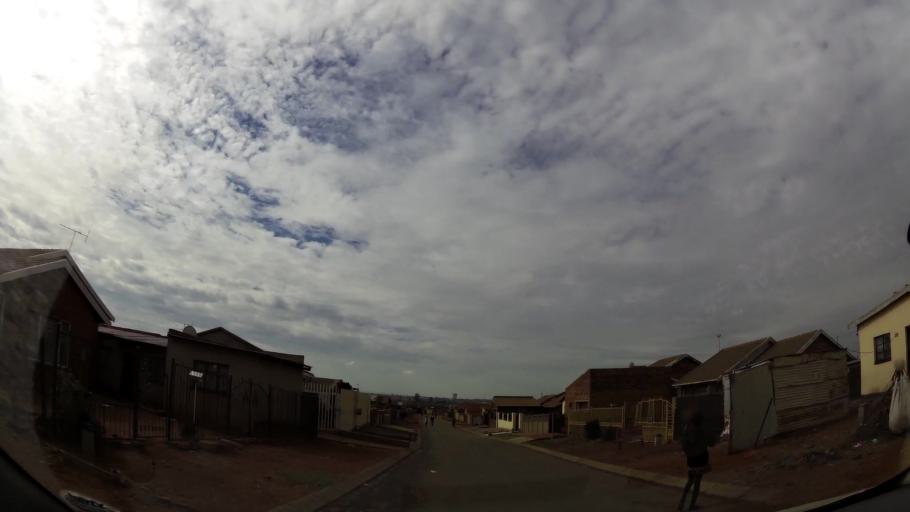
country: ZA
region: Gauteng
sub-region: Ekurhuleni Metropolitan Municipality
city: Germiston
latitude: -26.3756
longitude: 28.1662
